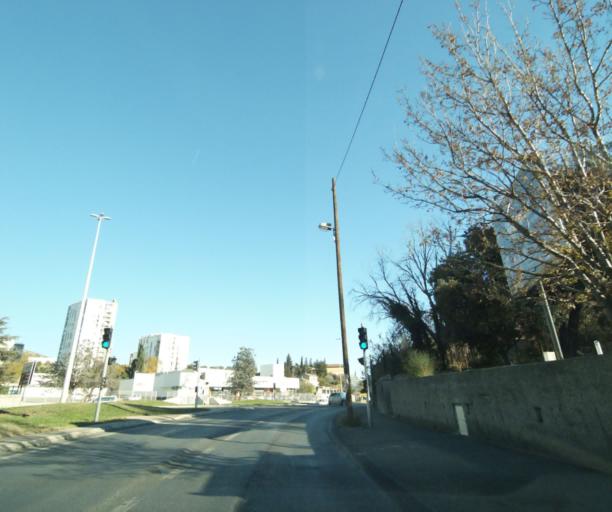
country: FR
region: Provence-Alpes-Cote d'Azur
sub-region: Departement des Bouches-du-Rhone
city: Marseille 14
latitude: 43.3489
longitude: 5.3749
